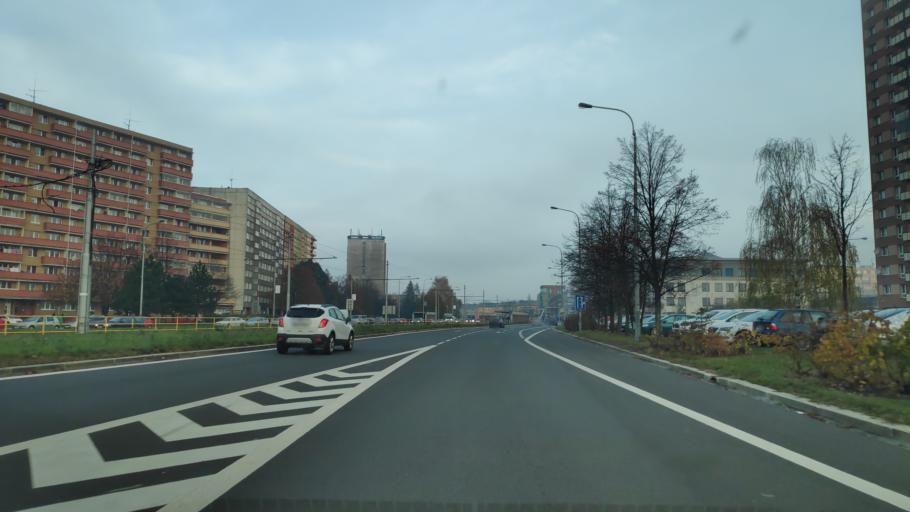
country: CZ
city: Vratimov
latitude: 49.7850
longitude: 18.2566
